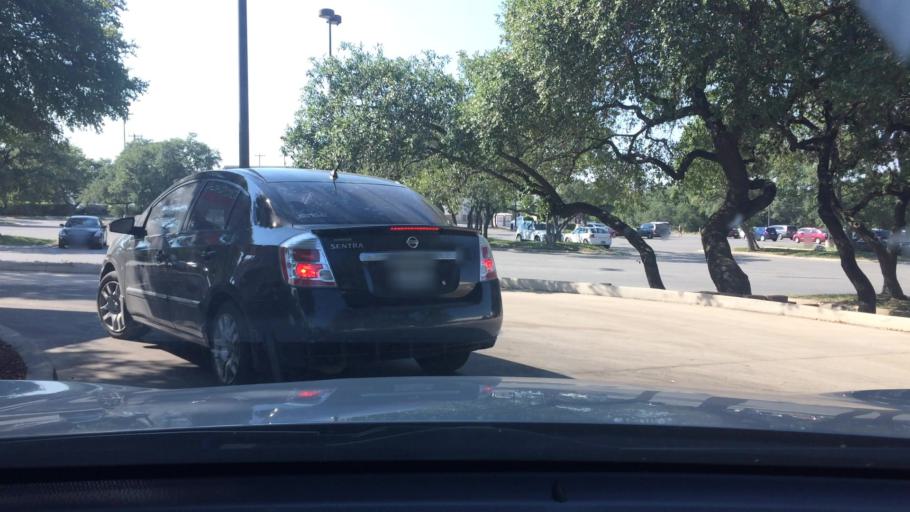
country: US
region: Texas
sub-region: Bexar County
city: Hollywood Park
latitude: 29.6111
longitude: -98.5077
